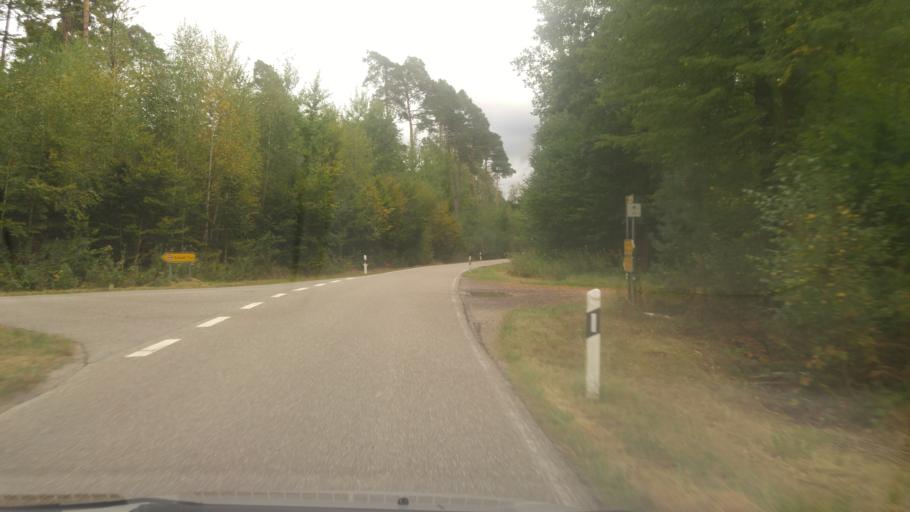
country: DE
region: Rheinland-Pfalz
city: Scheibenhardt
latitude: 48.9923
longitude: 8.1043
